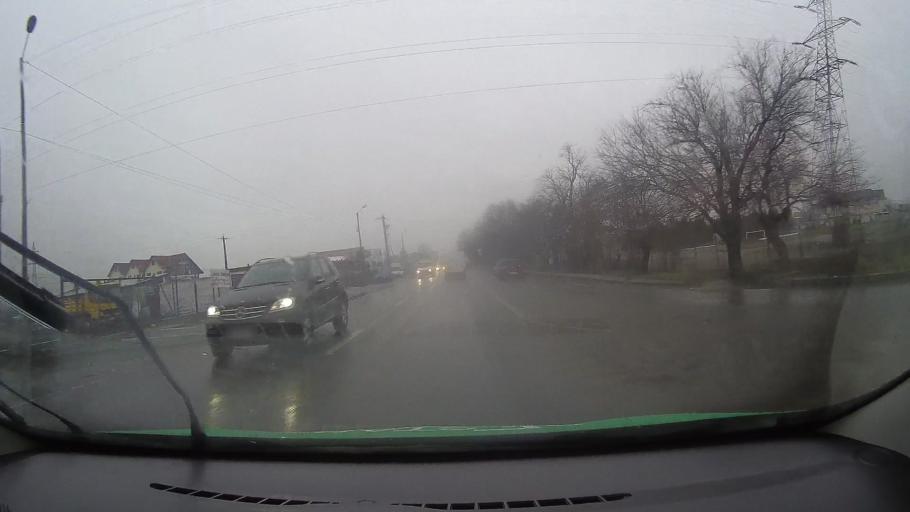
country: RO
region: Sibiu
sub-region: Municipiul Sibiu
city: Sibiu
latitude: 45.8203
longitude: 24.1507
